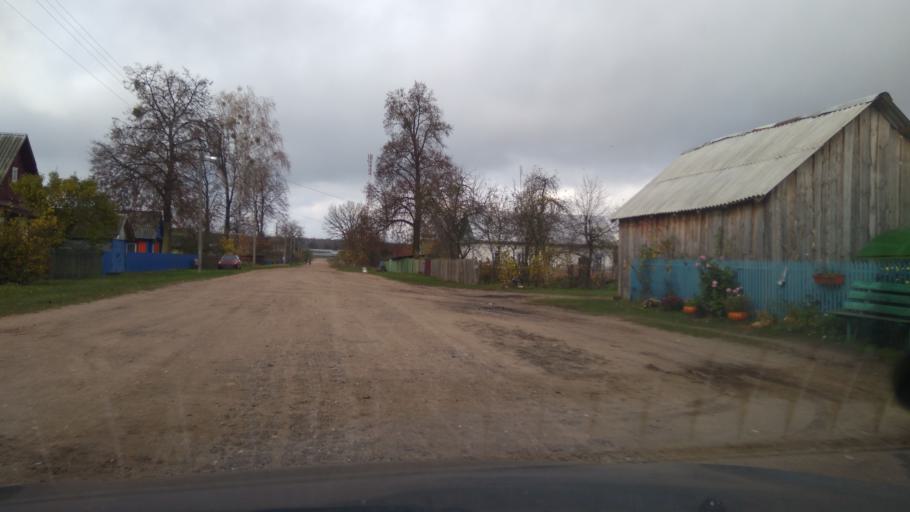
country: BY
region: Minsk
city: Staryya Darohi
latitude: 53.2029
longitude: 28.0443
